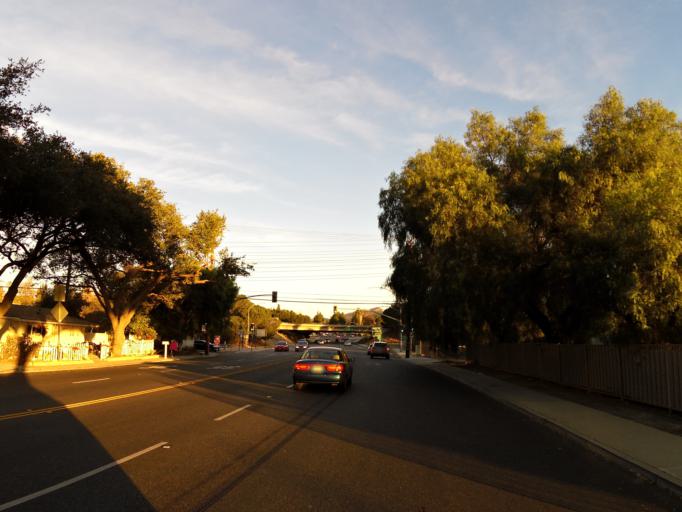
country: US
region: California
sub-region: Ventura County
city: Thousand Oaks
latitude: 34.2117
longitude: -118.8514
